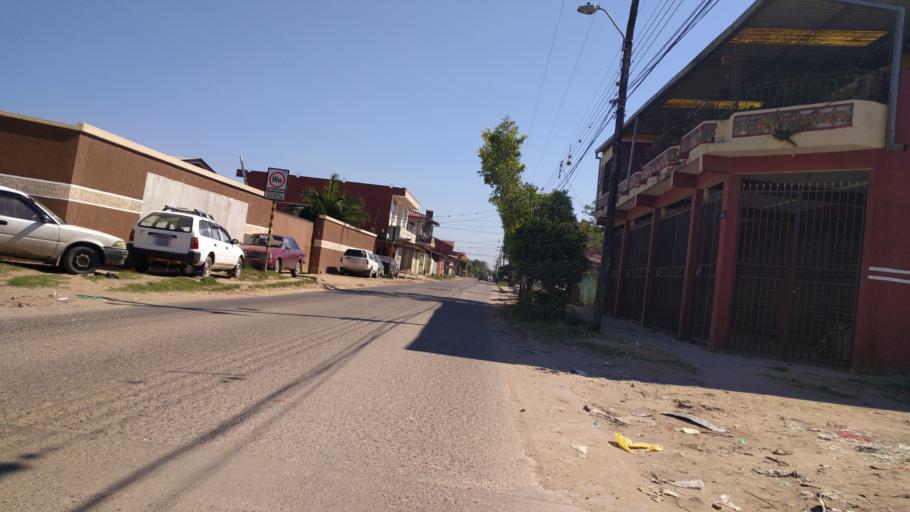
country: BO
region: Santa Cruz
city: Santa Cruz de la Sierra
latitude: -17.8326
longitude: -63.2251
